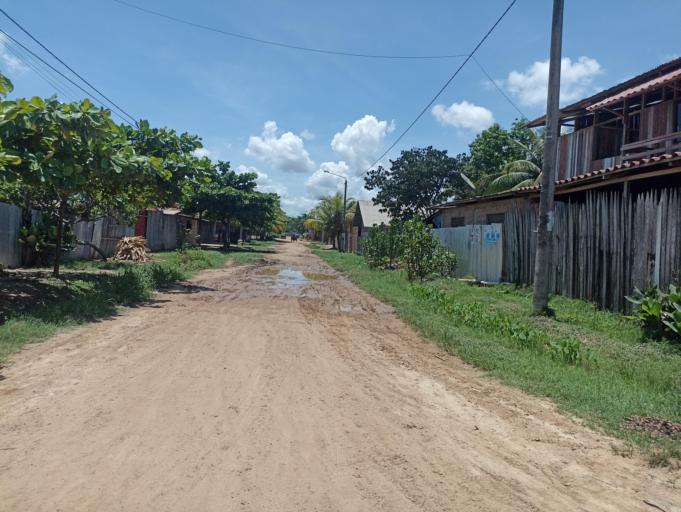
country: PE
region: Ucayali
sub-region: Provincia de Coronel Portillo
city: Puerto Callao
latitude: -8.3609
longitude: -74.5914
